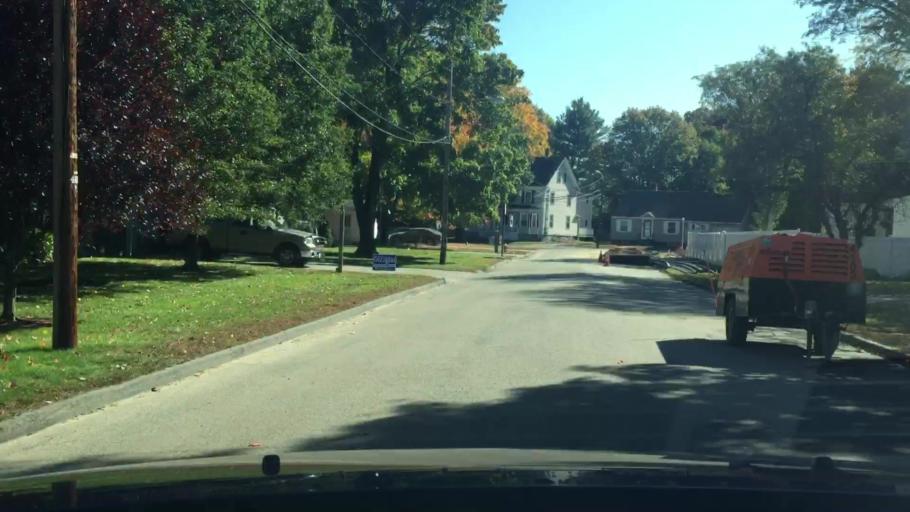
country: US
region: Massachusetts
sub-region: Essex County
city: North Andover
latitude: 42.6973
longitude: -71.1230
